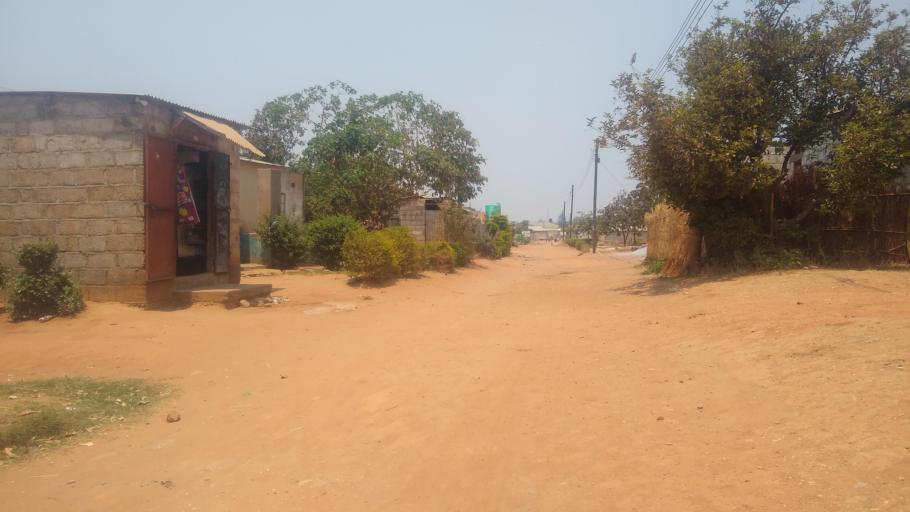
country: ZM
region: Lusaka
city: Lusaka
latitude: -15.4356
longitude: 28.3773
